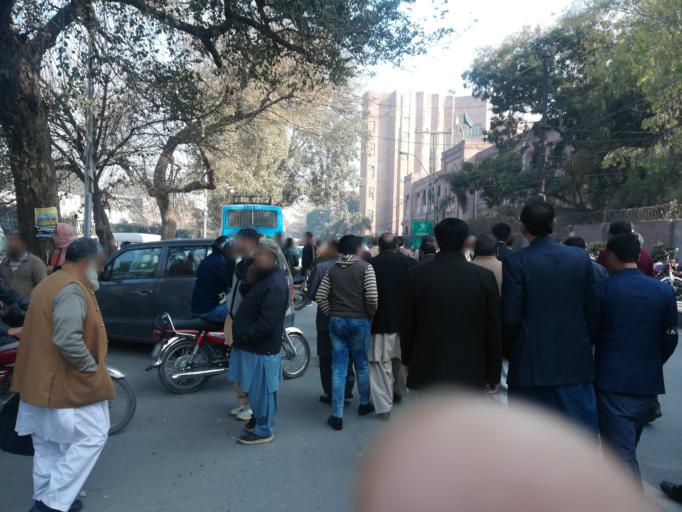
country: PK
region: Punjab
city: Lahore
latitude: 31.5667
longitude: 74.3062
